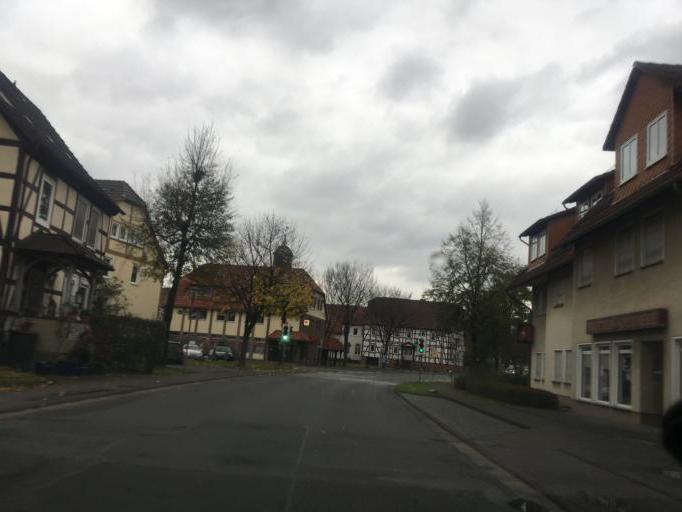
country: DE
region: Lower Saxony
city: Bodenfelde
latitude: 51.5988
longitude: 9.5497
